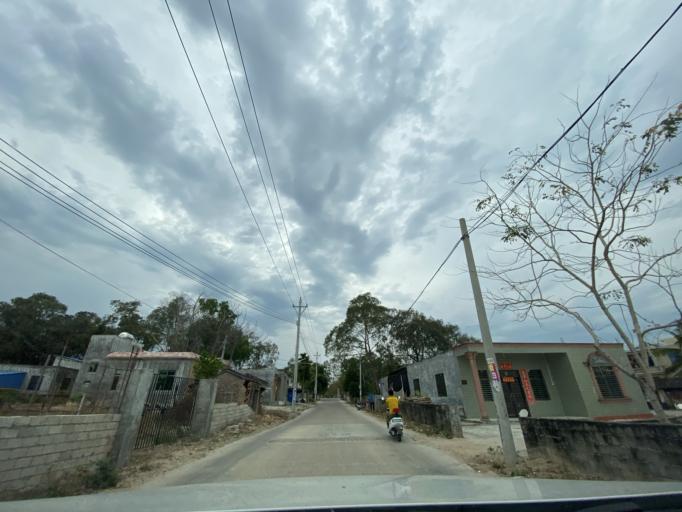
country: CN
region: Hainan
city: Yingzhou
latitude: 18.4190
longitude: 109.8226
